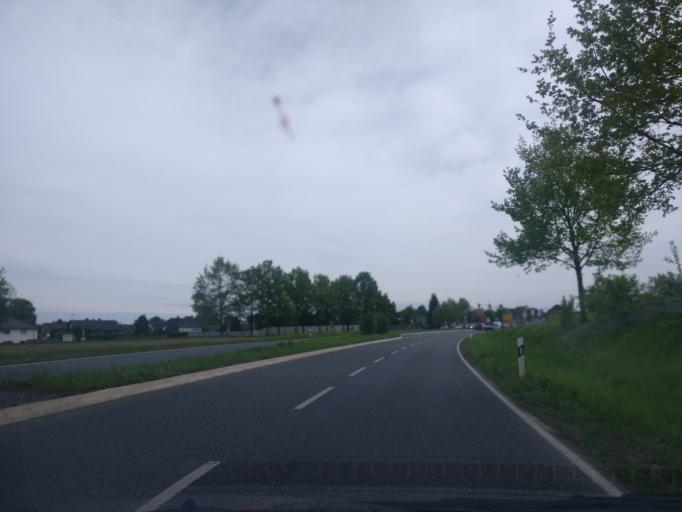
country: DE
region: Hesse
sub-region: Regierungsbezirk Kassel
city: Kassel
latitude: 51.3449
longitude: 9.5196
